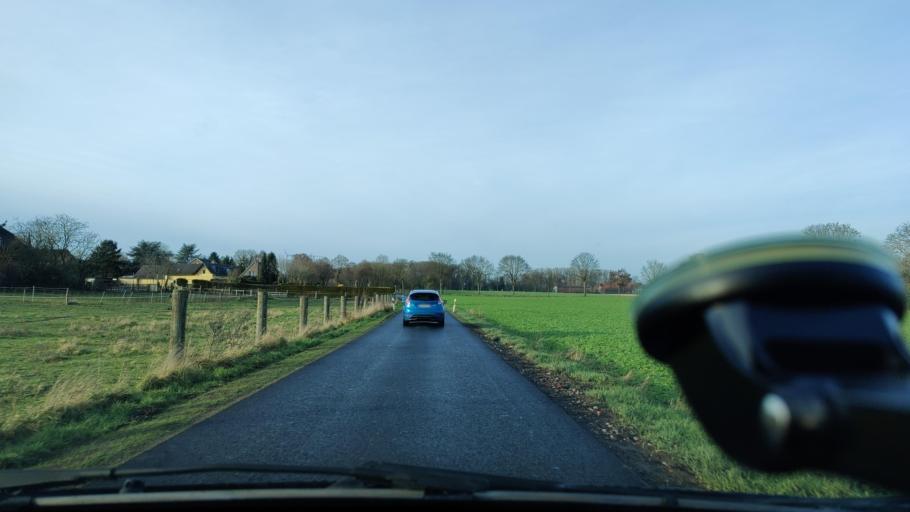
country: DE
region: North Rhine-Westphalia
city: Rees
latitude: 51.7228
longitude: 6.3563
